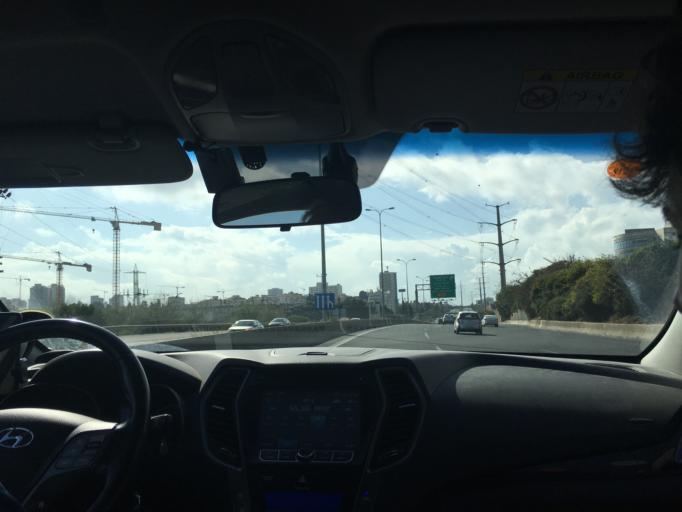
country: IL
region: Tel Aviv
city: Giv`at Shemu'el
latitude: 32.0860
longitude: 34.8457
